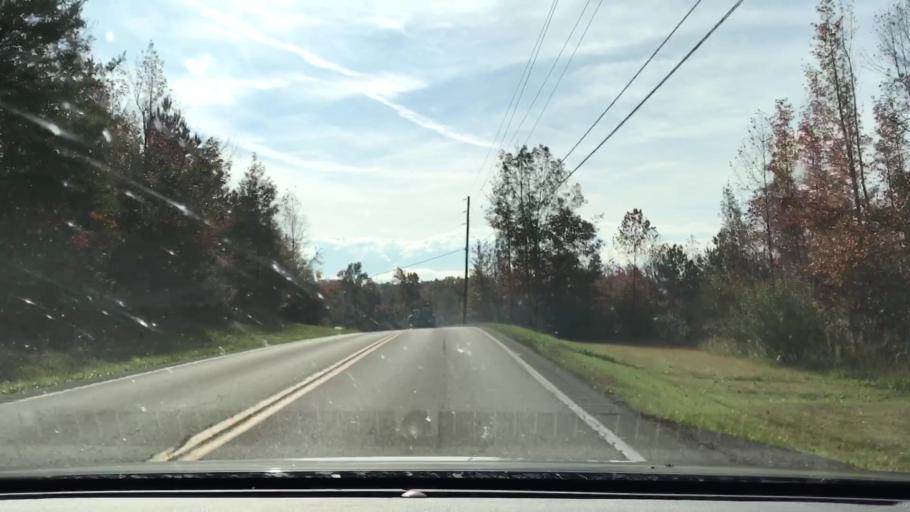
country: US
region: Tennessee
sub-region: Scott County
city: Huntsville
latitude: 36.3367
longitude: -84.6102
